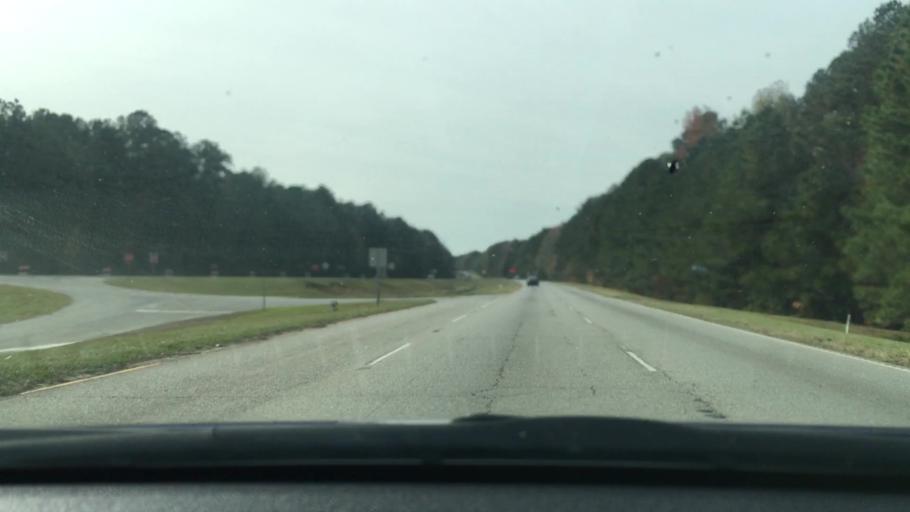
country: US
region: South Carolina
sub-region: Sumter County
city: Stateburg
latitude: 33.9470
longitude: -80.6328
